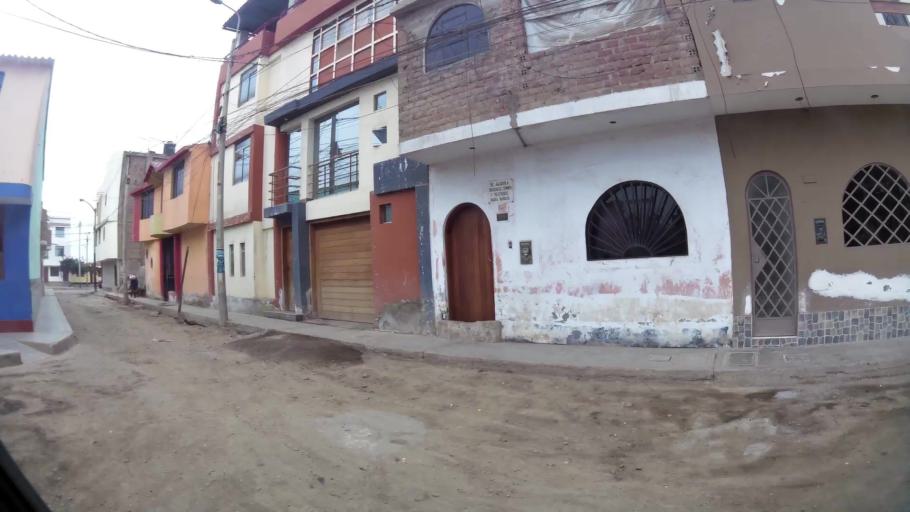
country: PE
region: La Libertad
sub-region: Provincia de Trujillo
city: Buenos Aires
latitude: -8.1427
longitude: -79.0494
